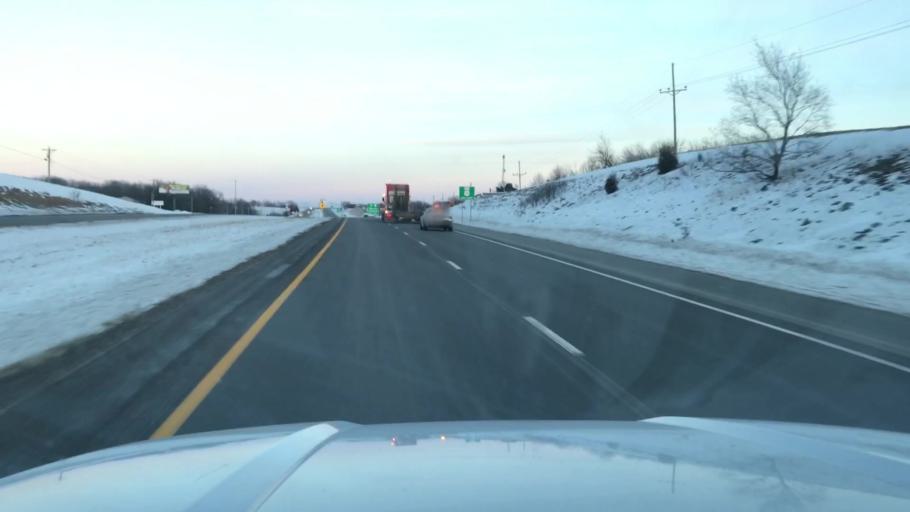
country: US
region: Missouri
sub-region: Clinton County
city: Cameron
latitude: 39.7538
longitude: -94.2594
